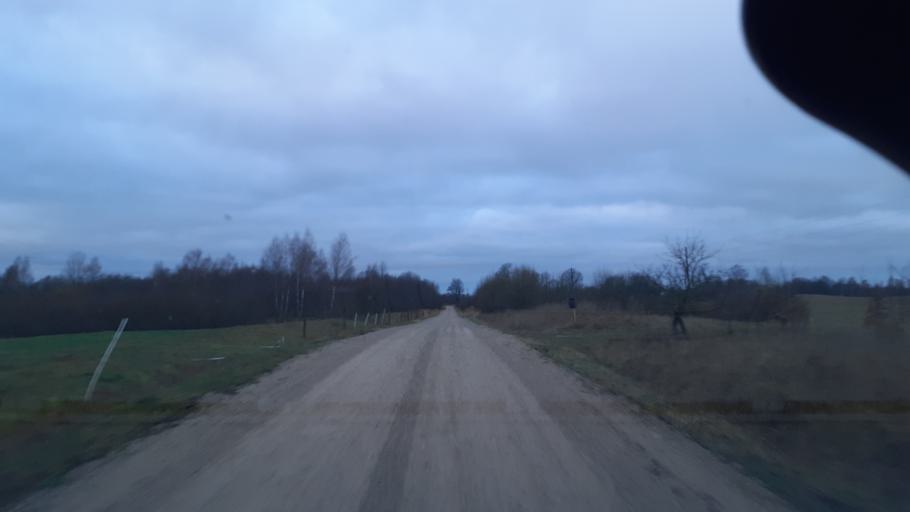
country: LV
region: Alsunga
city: Alsunga
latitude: 56.9042
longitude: 21.6901
